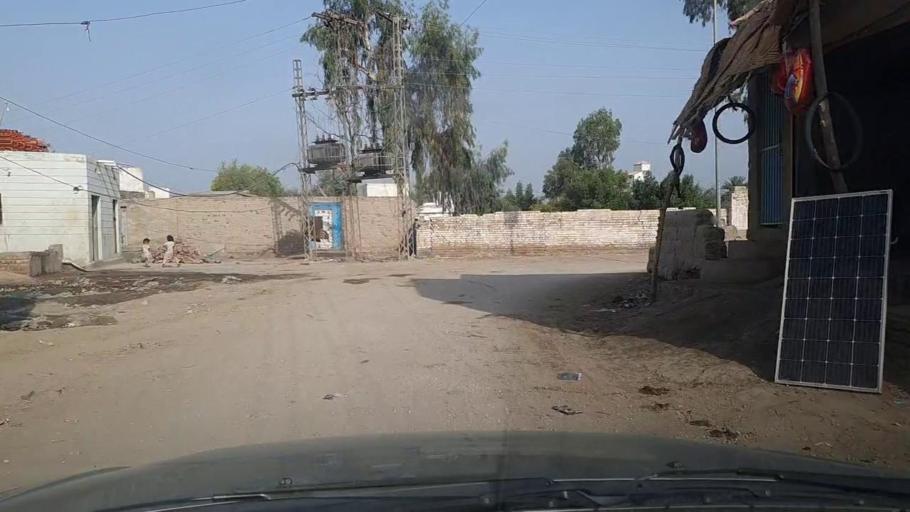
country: PK
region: Sindh
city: Pir jo Goth
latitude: 27.5560
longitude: 68.5514
